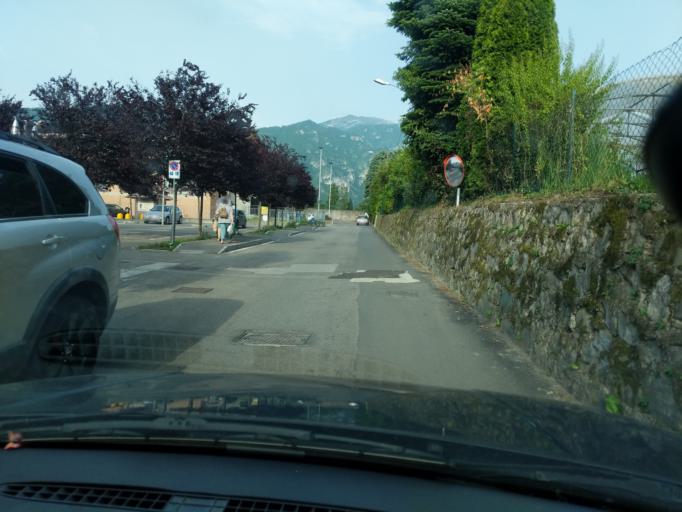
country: IT
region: Lombardy
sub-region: Provincia di Como
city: Bellagio
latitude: 45.9767
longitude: 9.2588
